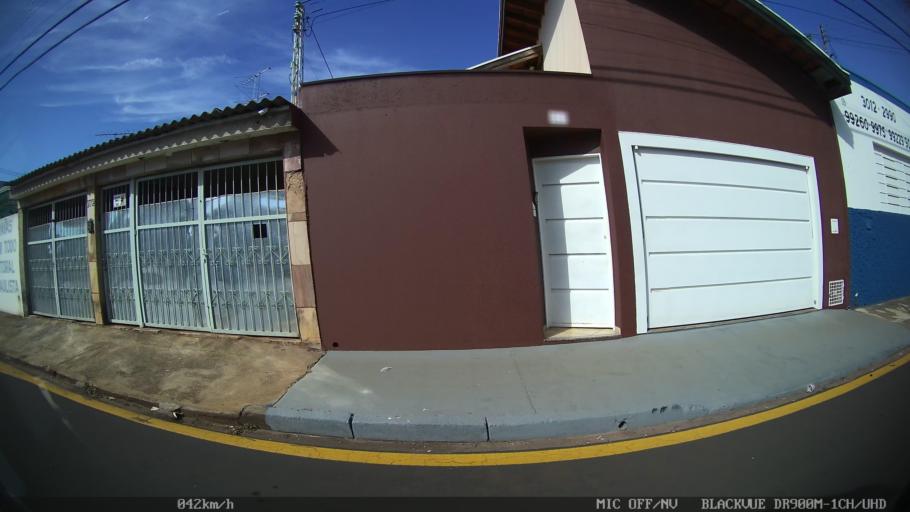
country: BR
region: Sao Paulo
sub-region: Franca
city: Franca
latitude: -20.5348
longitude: -47.4169
